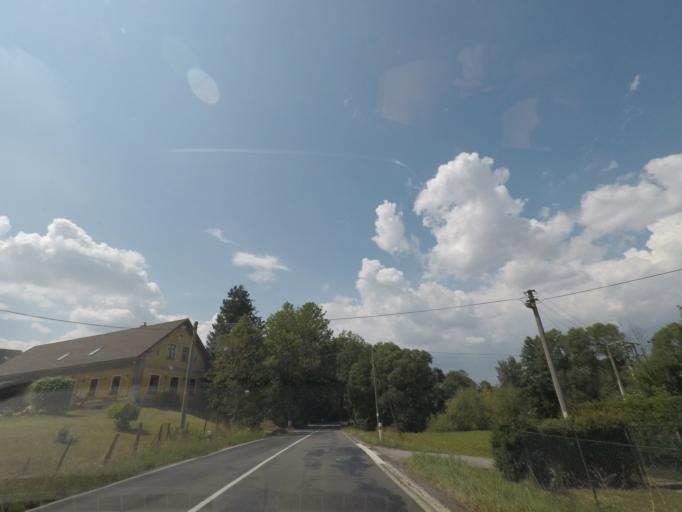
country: CZ
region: Kralovehradecky
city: Zadni Mostek
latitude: 50.5259
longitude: 15.6921
